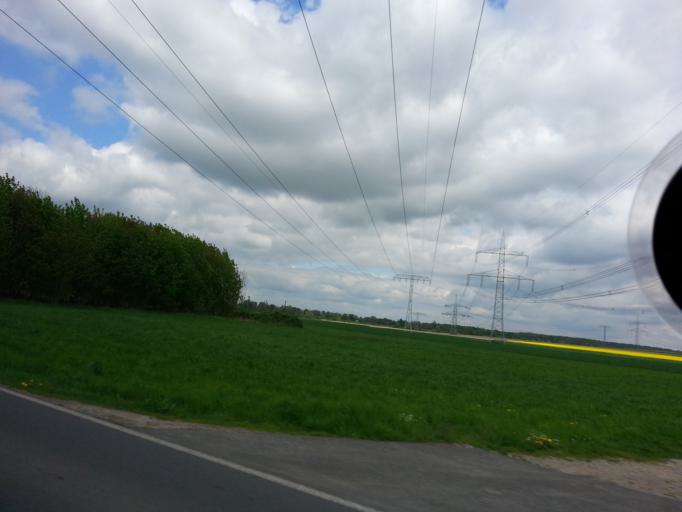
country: DE
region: Brandenburg
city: Altlandsberg
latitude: 52.5532
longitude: 13.7397
